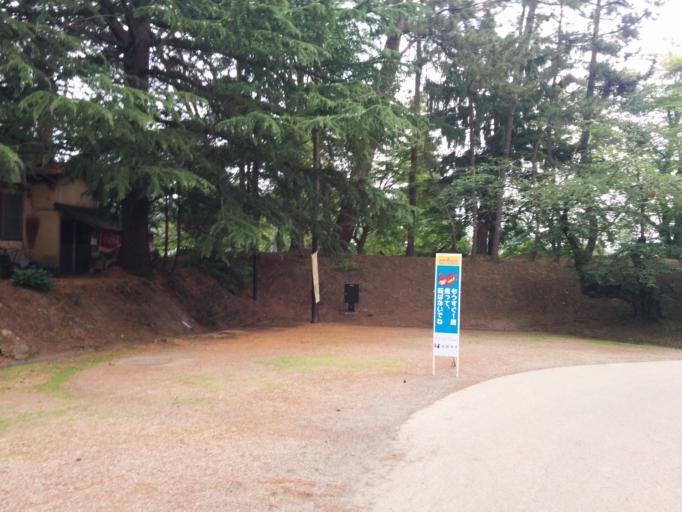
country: JP
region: Aomori
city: Hirosaki
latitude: 40.6098
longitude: 140.4660
